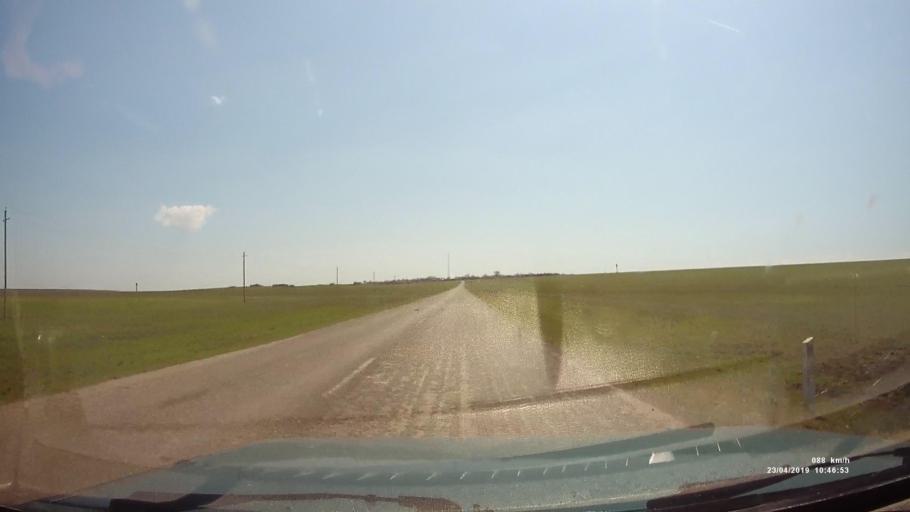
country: RU
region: Kalmykiya
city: Yashalta
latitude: 46.4394
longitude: 42.6984
